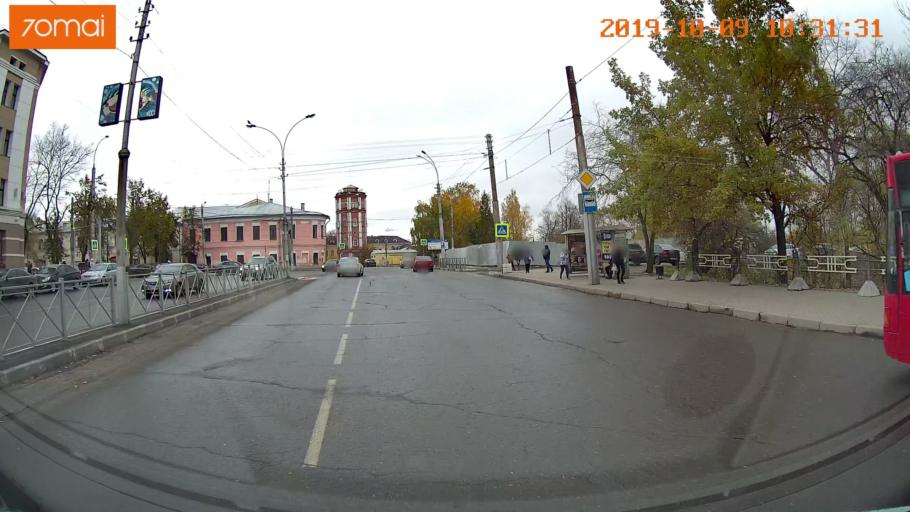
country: RU
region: Vologda
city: Vologda
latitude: 59.2224
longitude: 39.8929
